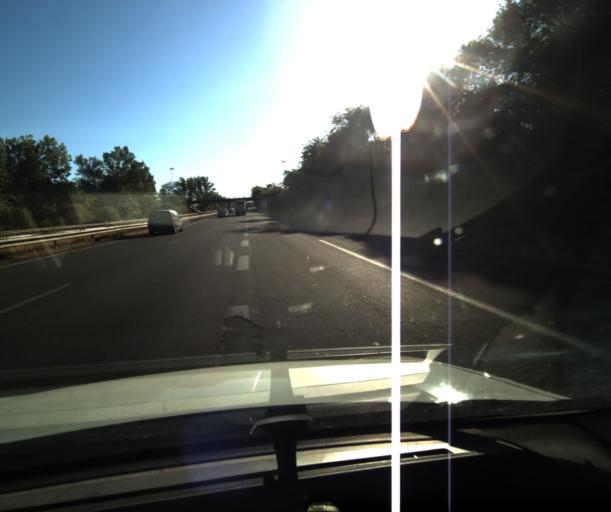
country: FR
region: Midi-Pyrenees
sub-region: Departement du Tarn-et-Garonne
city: Castelsarrasin
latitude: 44.0535
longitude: 1.0981
